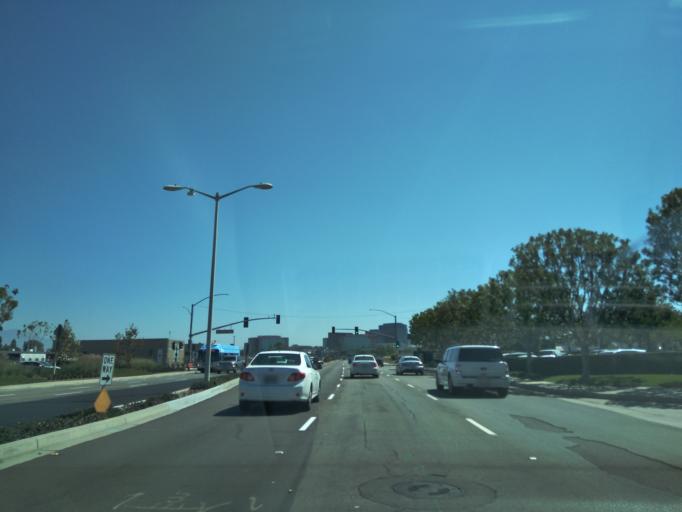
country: US
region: California
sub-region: Orange County
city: Irvine
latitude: 33.6887
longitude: -117.8637
